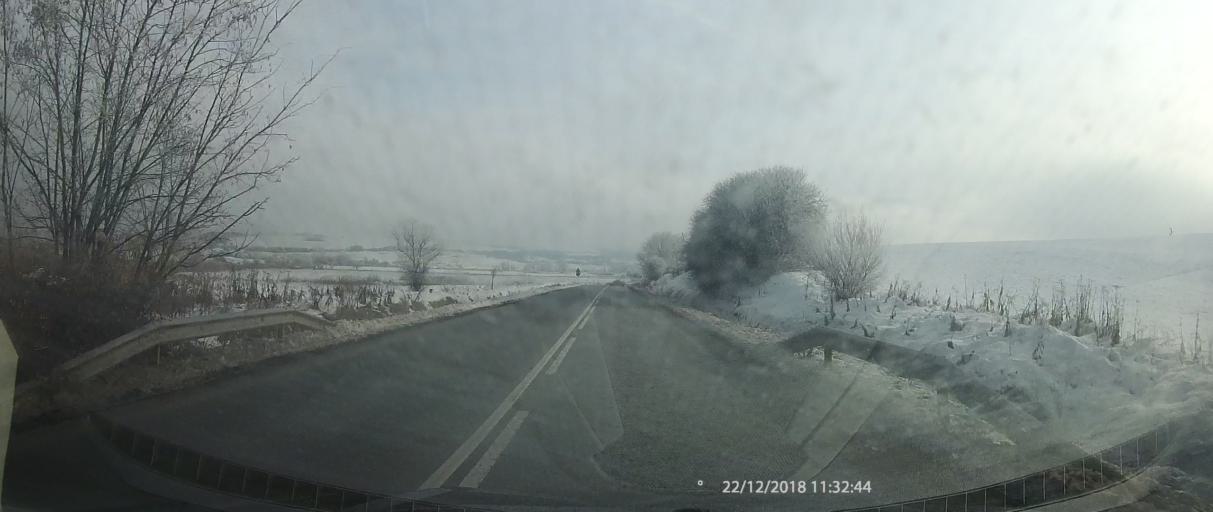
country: BG
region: Kyustendil
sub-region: Obshtina Dupnitsa
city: Dupnitsa
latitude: 42.2722
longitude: 23.0308
